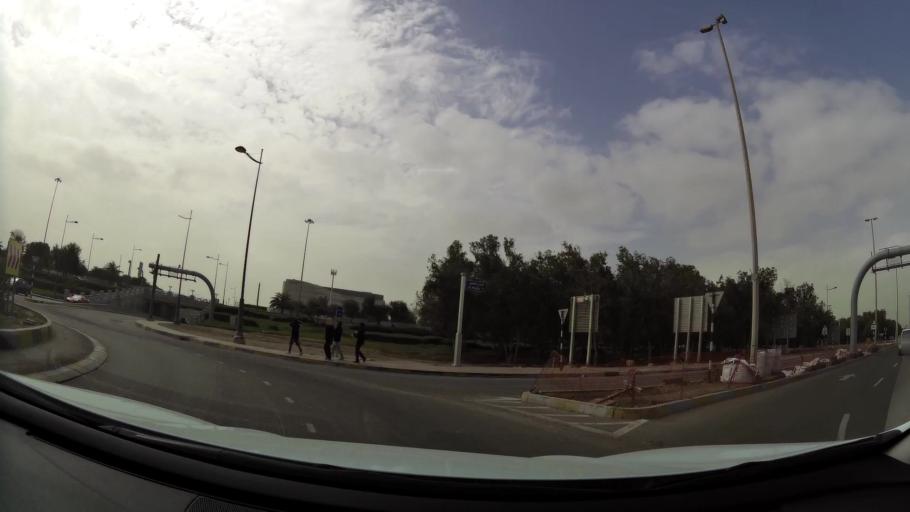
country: AE
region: Abu Dhabi
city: Abu Dhabi
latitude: 24.4001
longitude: 54.5027
